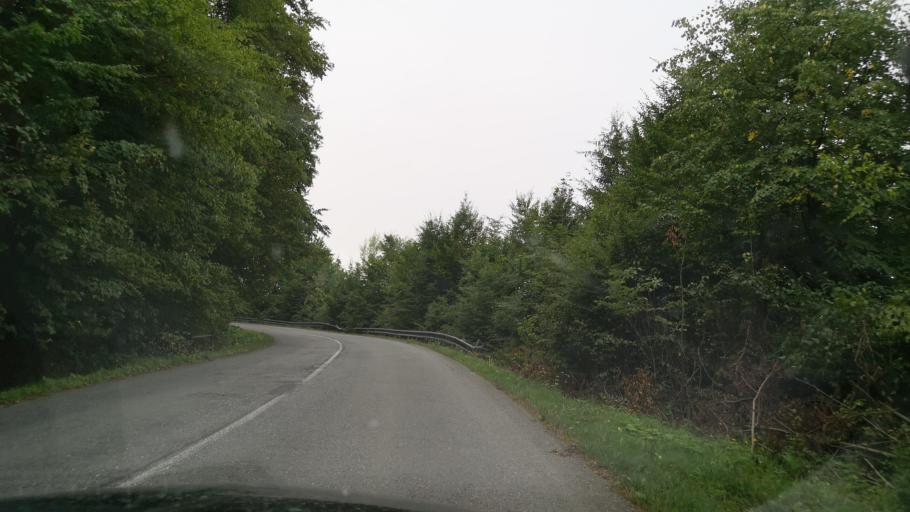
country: SK
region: Banskobystricky
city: Tisovec
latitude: 48.5773
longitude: 19.9739
